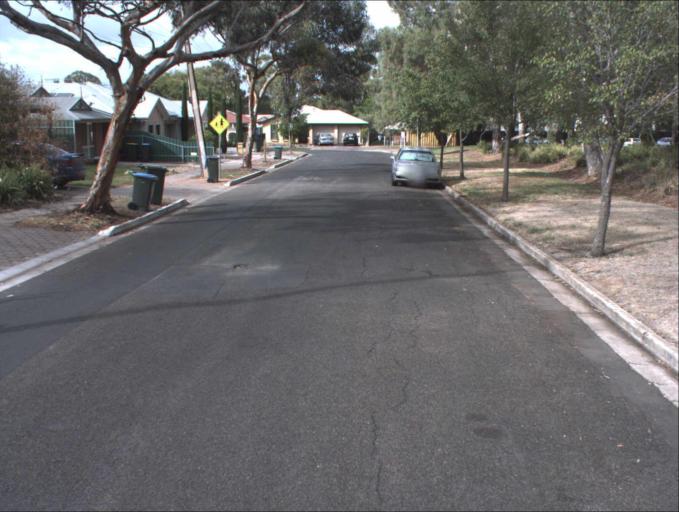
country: AU
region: South Australia
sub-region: Port Adelaide Enfield
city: Klemzig
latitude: -34.8648
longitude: 138.6399
